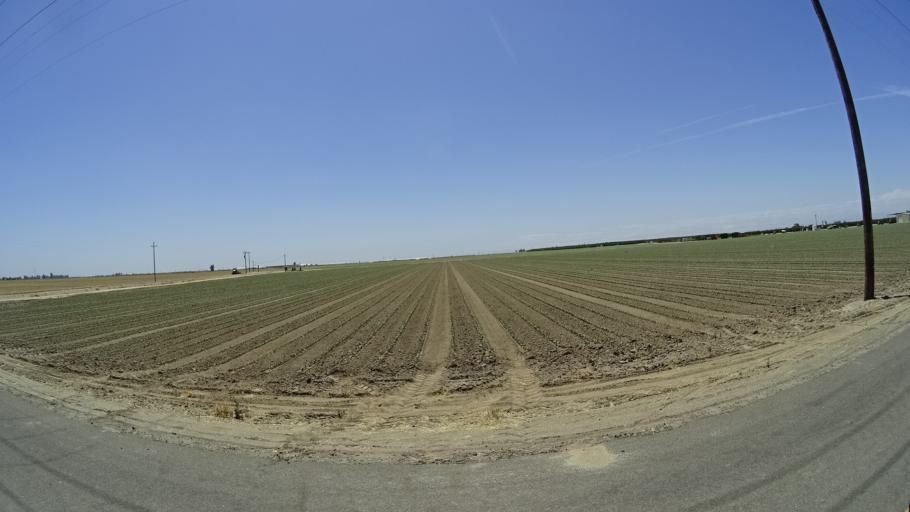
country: US
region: California
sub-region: Kings County
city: Armona
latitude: 36.2402
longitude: -119.6965
